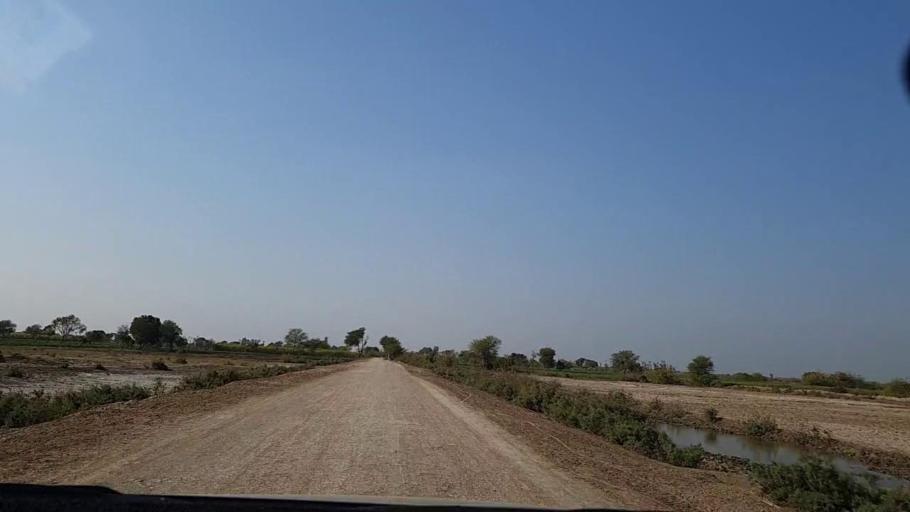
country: PK
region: Sindh
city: Digri
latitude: 25.1900
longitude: 68.9978
